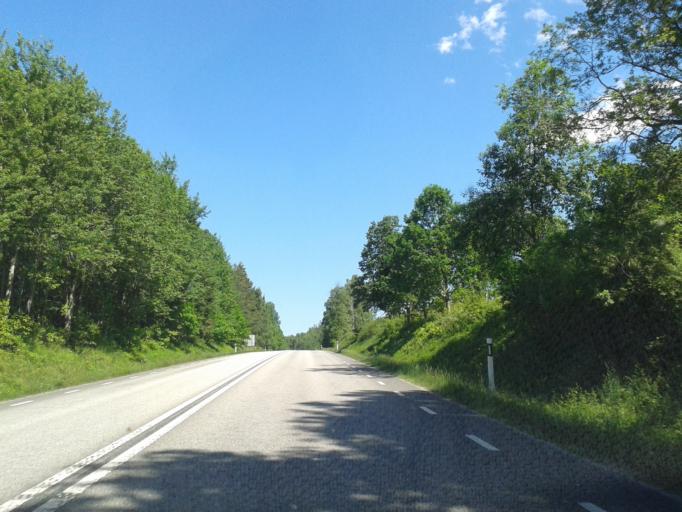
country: SE
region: Vaestra Goetaland
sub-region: Orust
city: Henan
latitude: 58.2857
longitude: 11.6995
